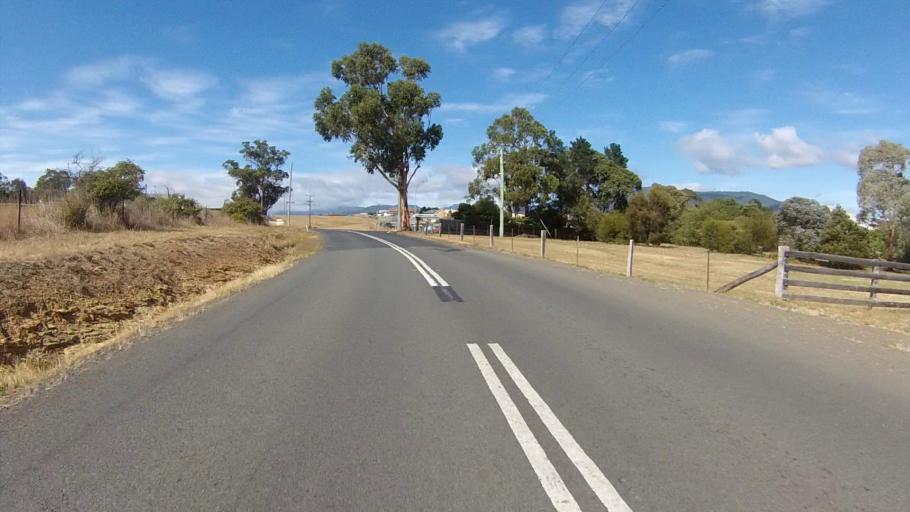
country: AU
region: Tasmania
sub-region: Brighton
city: Old Beach
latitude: -42.7456
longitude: 147.2816
